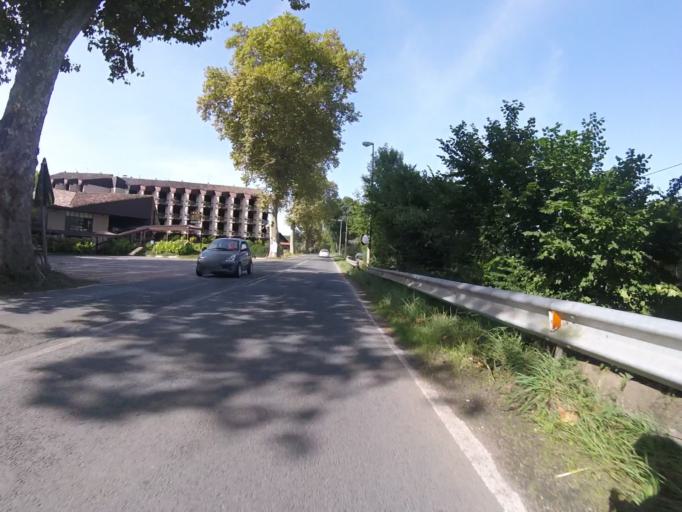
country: ES
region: Navarre
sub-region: Provincia de Navarra
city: Doneztebe
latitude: 43.1351
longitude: -1.5351
